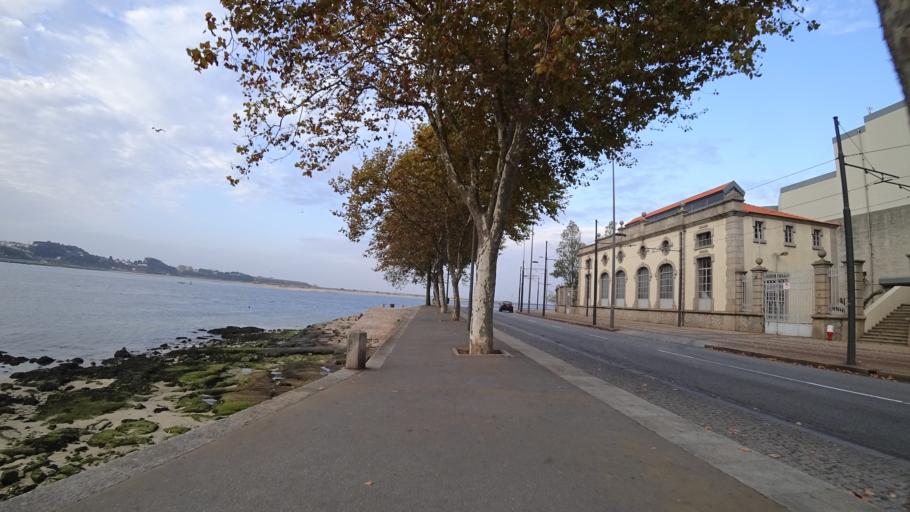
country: PT
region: Porto
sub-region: Vila Nova de Gaia
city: Canidelo
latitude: 41.1471
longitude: -8.6571
